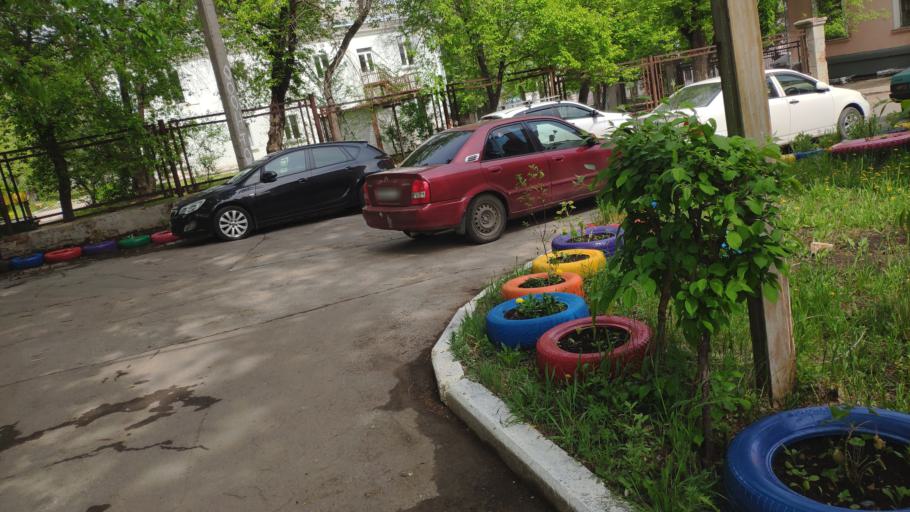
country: RU
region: Chelyabinsk
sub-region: Gorod Magnitogorsk
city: Magnitogorsk
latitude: 53.4214
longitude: 58.9563
